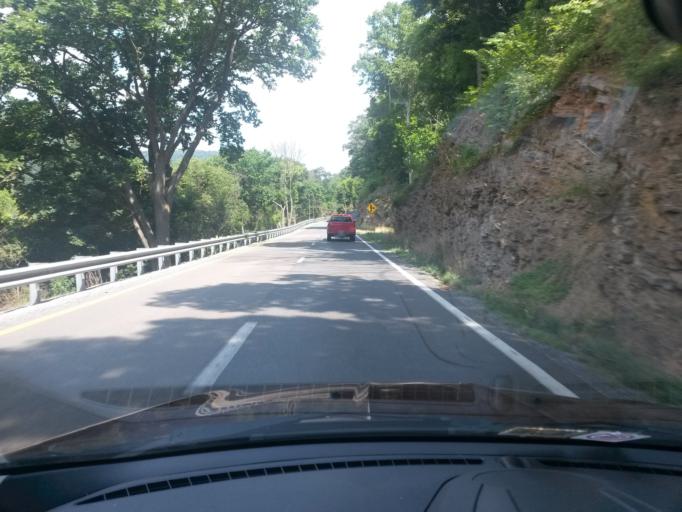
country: US
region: Virginia
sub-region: Giles County
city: Narrows
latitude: 37.3555
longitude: -80.8112
